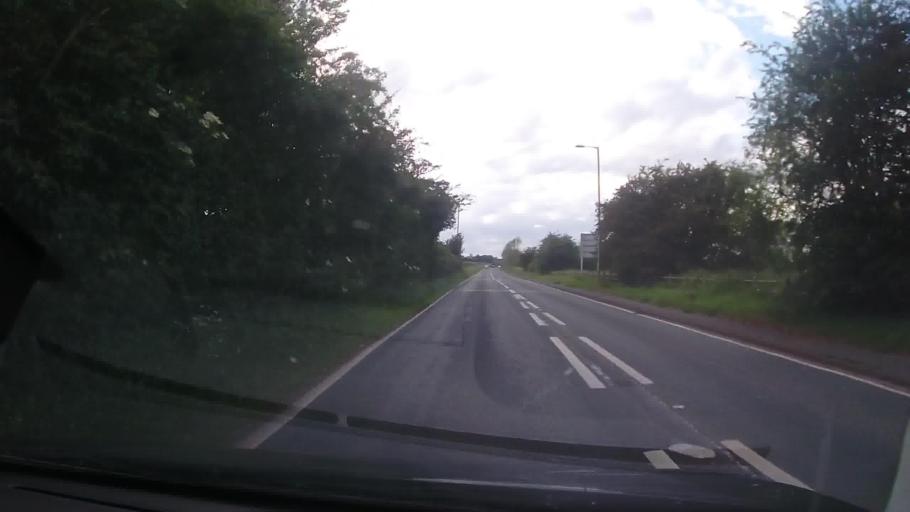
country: GB
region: England
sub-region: Shropshire
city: Berrington
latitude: 52.6796
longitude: -2.6837
